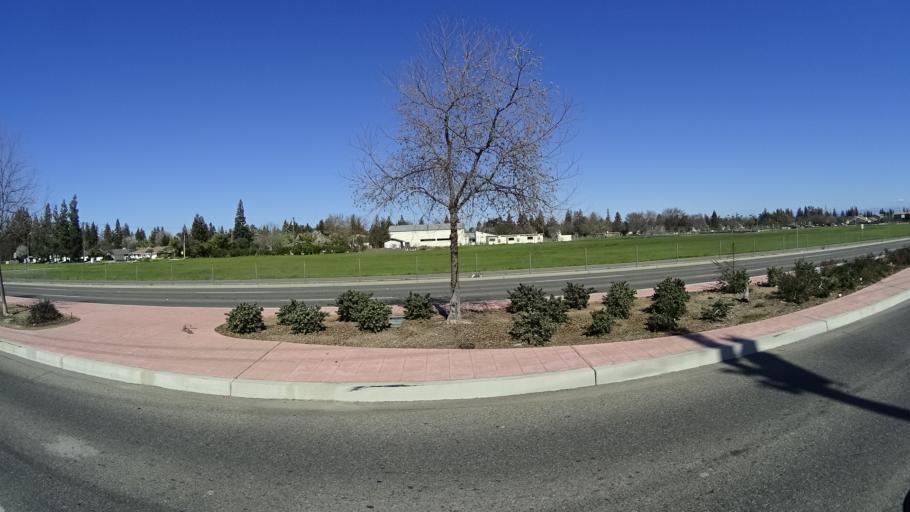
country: US
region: California
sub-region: Fresno County
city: Fresno
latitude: 36.8370
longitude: -119.8554
